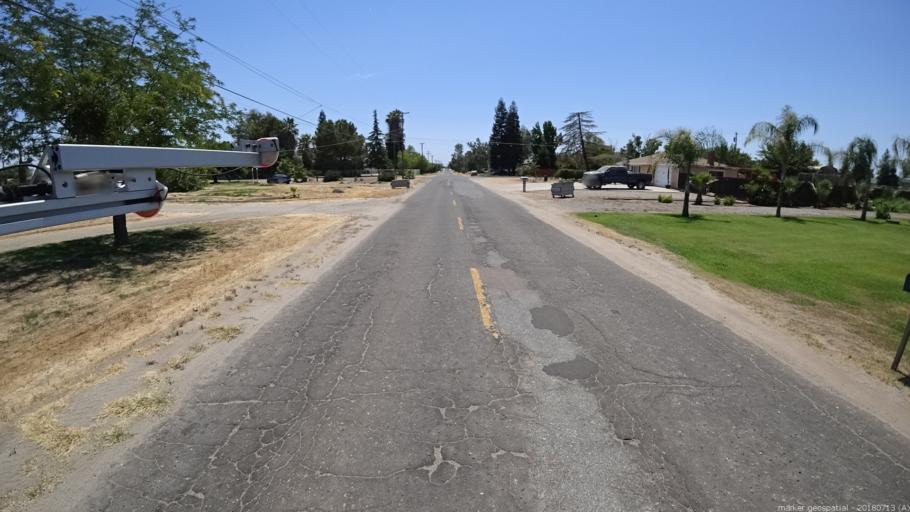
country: US
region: California
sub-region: Madera County
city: Madera Acres
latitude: 37.0115
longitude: -120.0768
